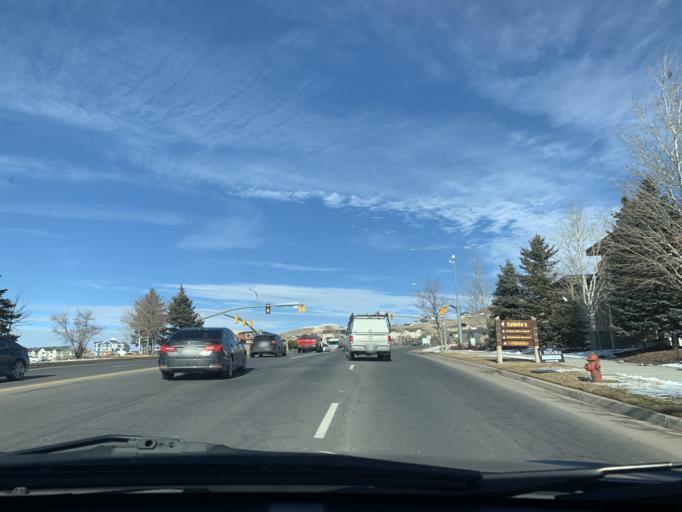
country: US
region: Utah
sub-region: Utah County
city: Lehi
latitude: 40.4338
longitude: -111.8810
